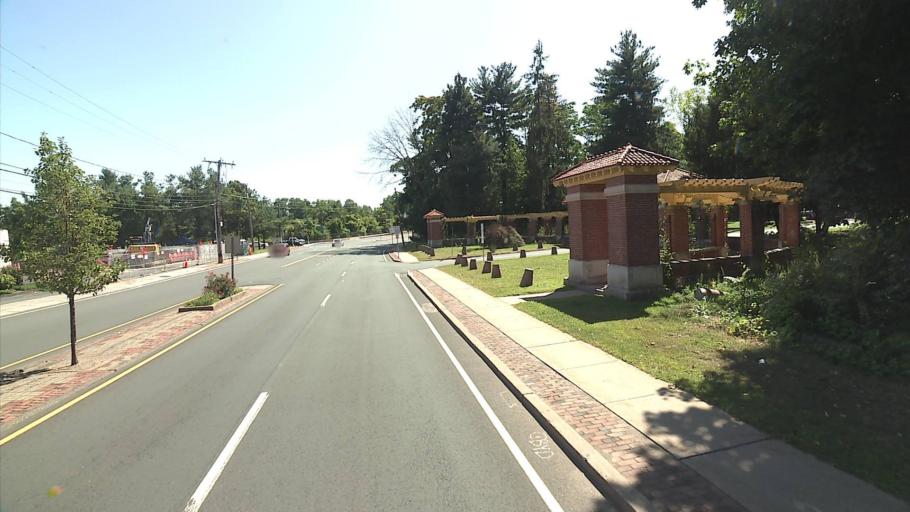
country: US
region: Connecticut
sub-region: Hartford County
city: Blue Hills
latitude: 41.8068
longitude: -72.6587
